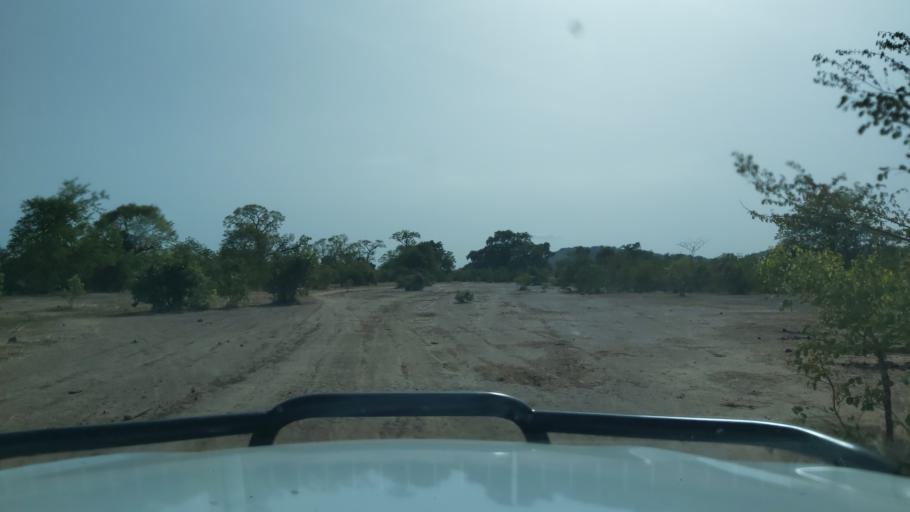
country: ML
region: Koulikoro
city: Koulikoro
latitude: 13.1763
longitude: -7.7522
